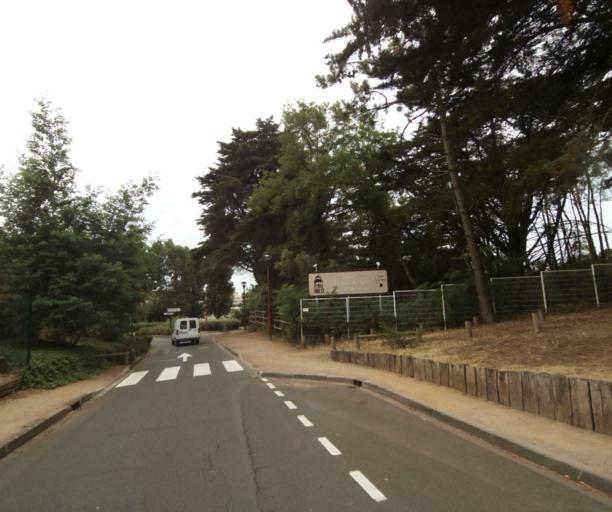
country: FR
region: Pays de la Loire
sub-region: Departement de la Vendee
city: Chateau-d'Olonne
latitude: 46.4841
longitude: -1.7588
